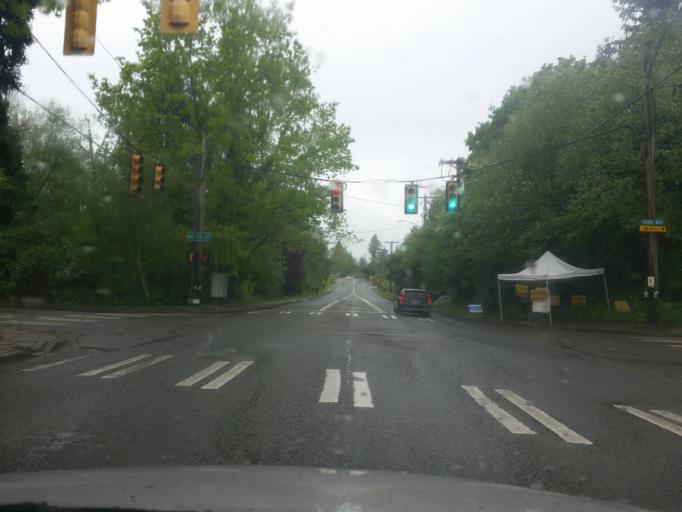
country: US
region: Washington
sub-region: King County
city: Inglewood-Finn Hill
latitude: 47.7404
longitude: -122.2243
